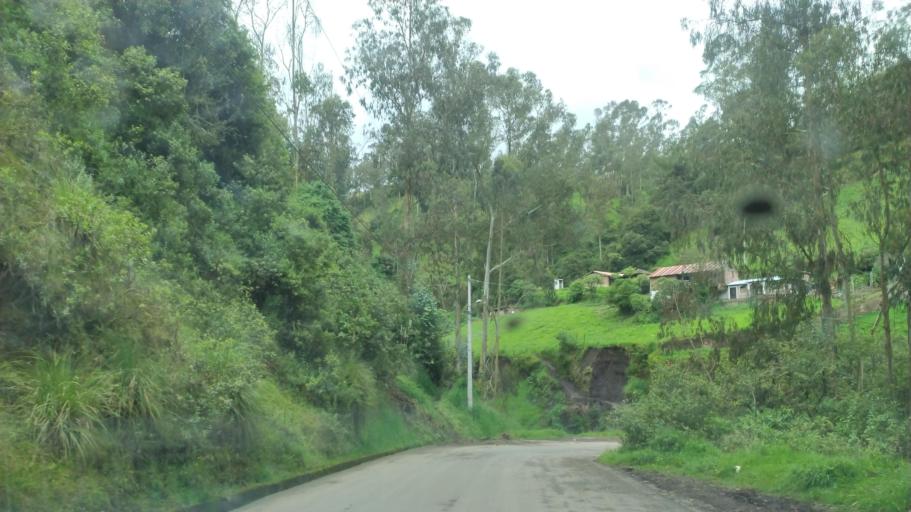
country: EC
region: Chimborazo
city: Riobamba
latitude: -1.6835
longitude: -78.5732
